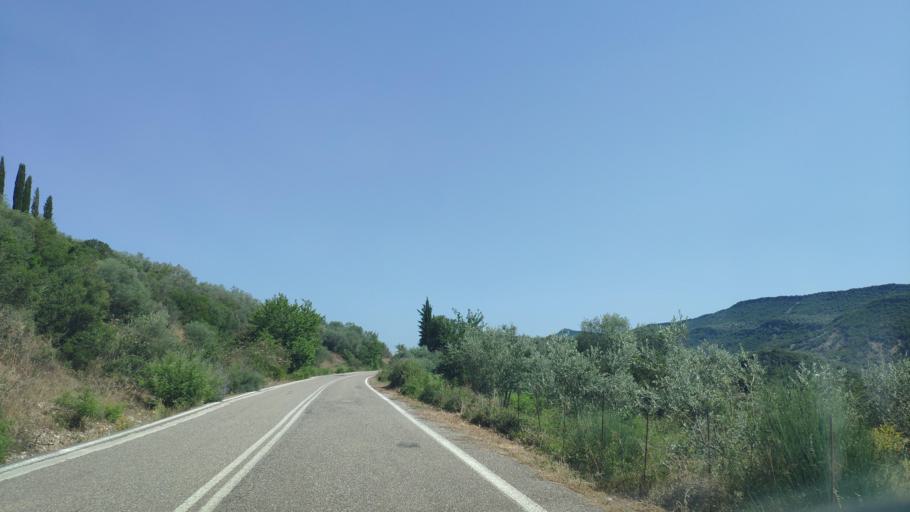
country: GR
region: West Greece
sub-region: Nomos Aitolias kai Akarnanias
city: Lepenou
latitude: 38.7466
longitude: 21.3437
